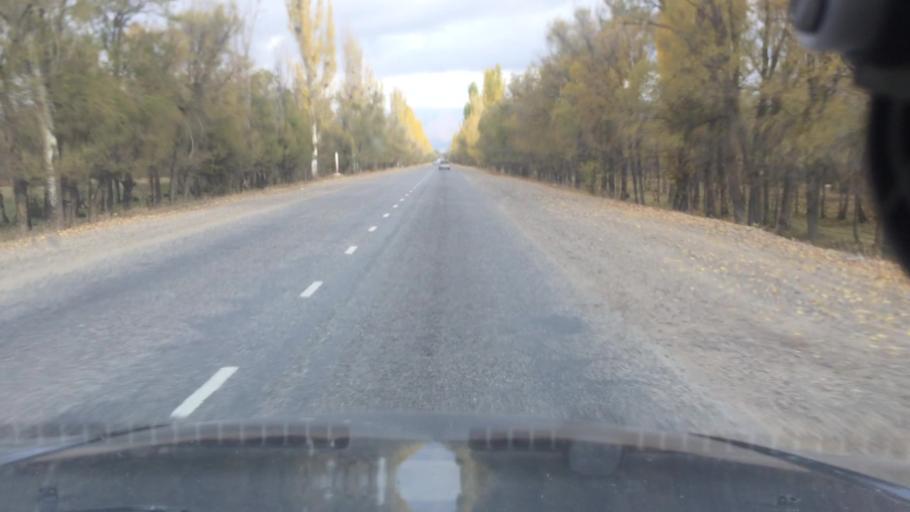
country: KG
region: Ysyk-Koel
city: Tyup
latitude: 42.6328
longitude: 78.3599
